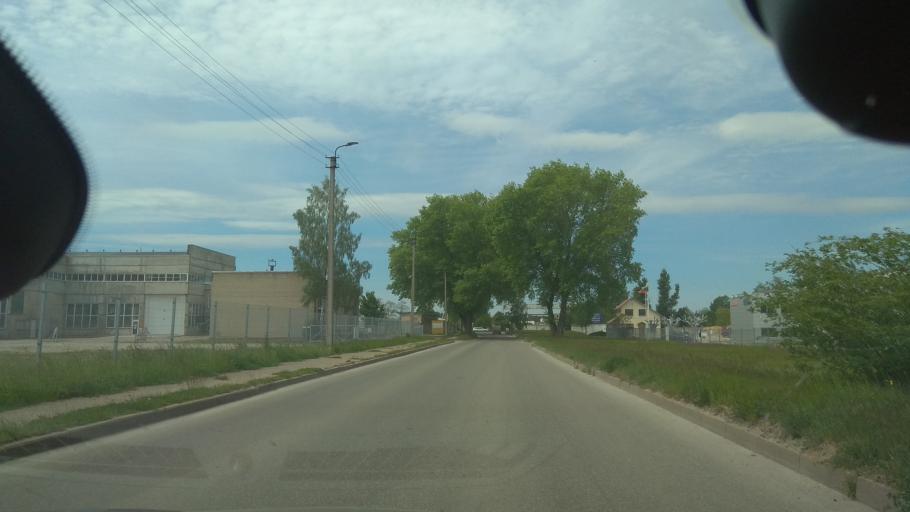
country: LT
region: Kauno apskritis
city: Jonava
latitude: 55.0909
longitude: 24.2835
